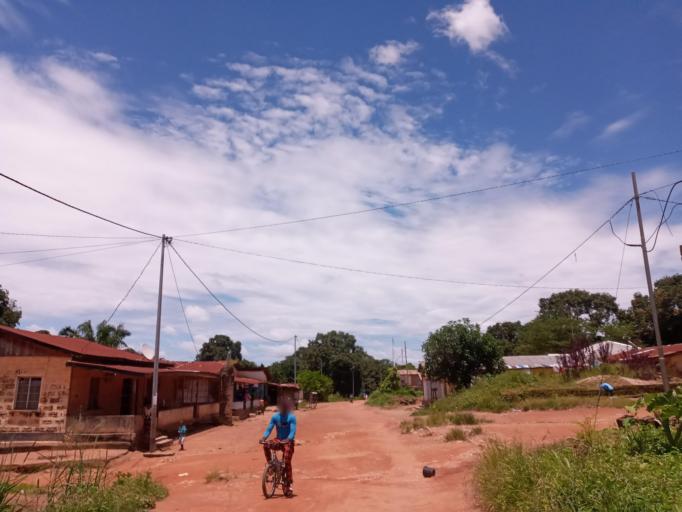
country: SL
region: Eastern Province
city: Koidu
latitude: 8.6475
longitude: -10.9637
